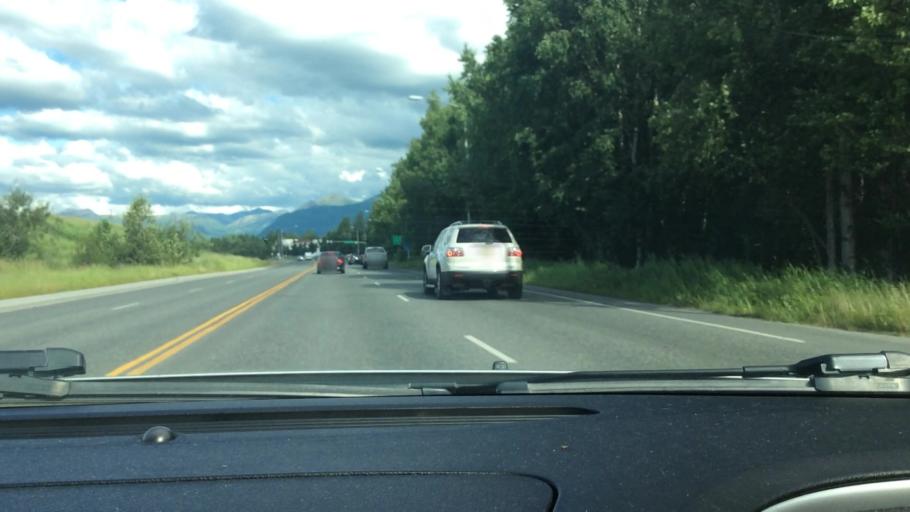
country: US
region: Alaska
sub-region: Anchorage Municipality
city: Anchorage
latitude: 61.2077
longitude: -149.8448
